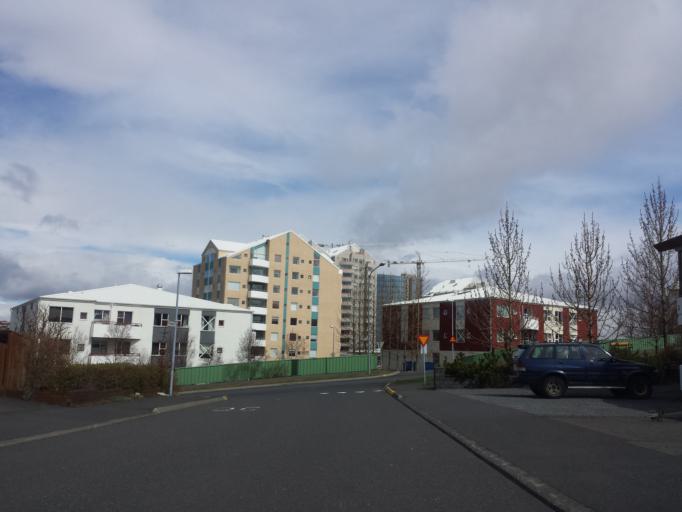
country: IS
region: Capital Region
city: Kopavogur
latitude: 64.1014
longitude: -21.8941
